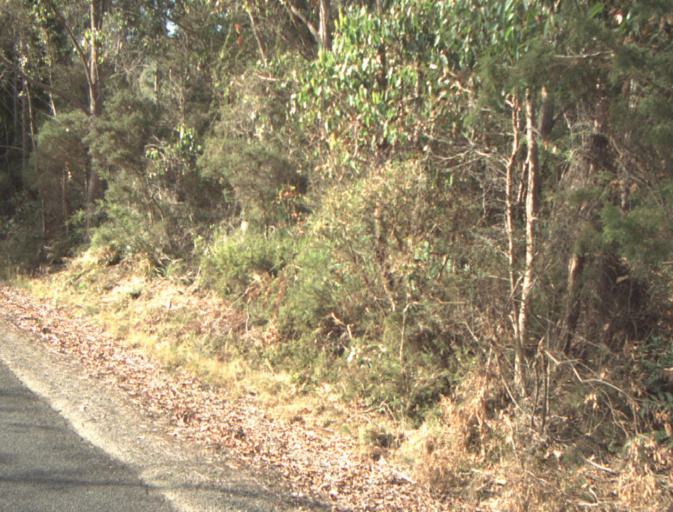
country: AU
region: Tasmania
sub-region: Launceston
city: Mayfield
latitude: -41.2688
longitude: 147.1616
